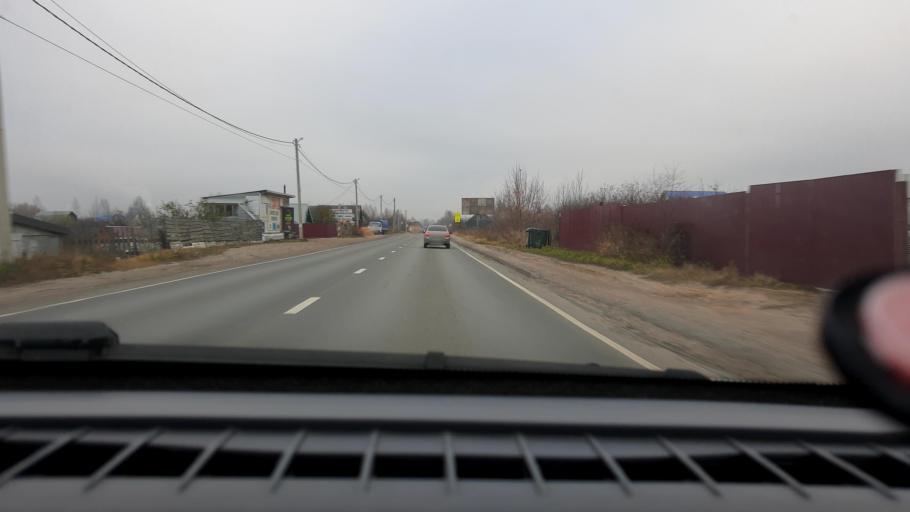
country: RU
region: Nizjnij Novgorod
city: Gidrotorf
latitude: 56.5457
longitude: 43.5268
